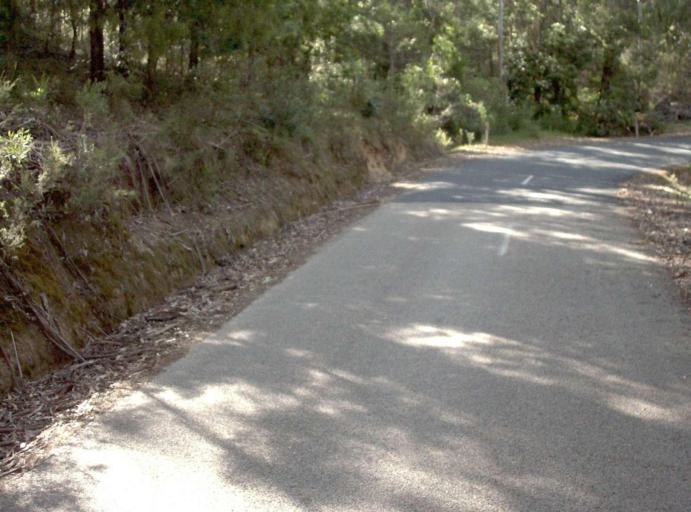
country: AU
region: Victoria
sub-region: East Gippsland
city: Lakes Entrance
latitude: -37.4408
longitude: 148.5905
